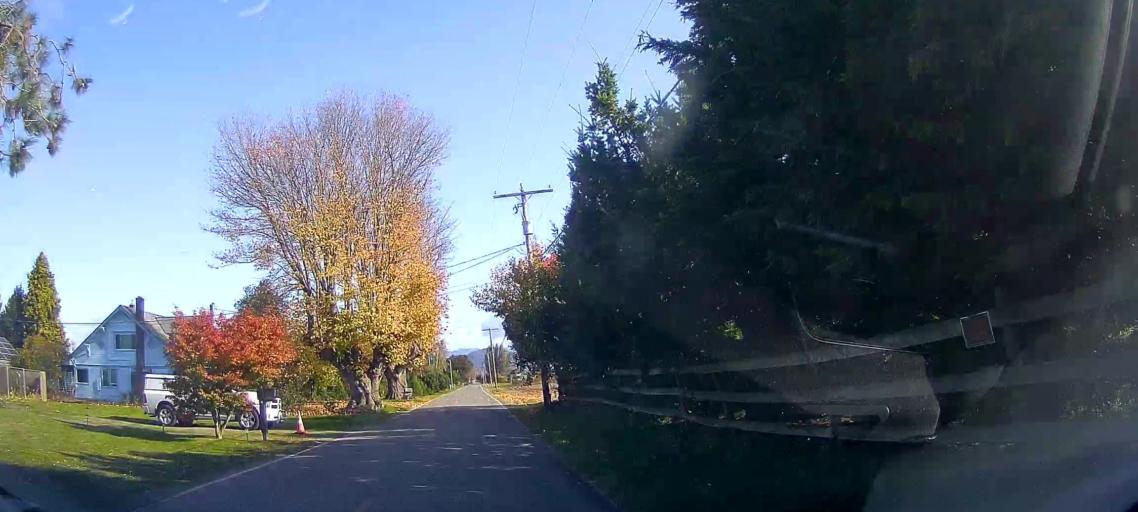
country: US
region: Washington
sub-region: Skagit County
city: Mount Vernon
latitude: 48.3992
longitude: -122.3928
